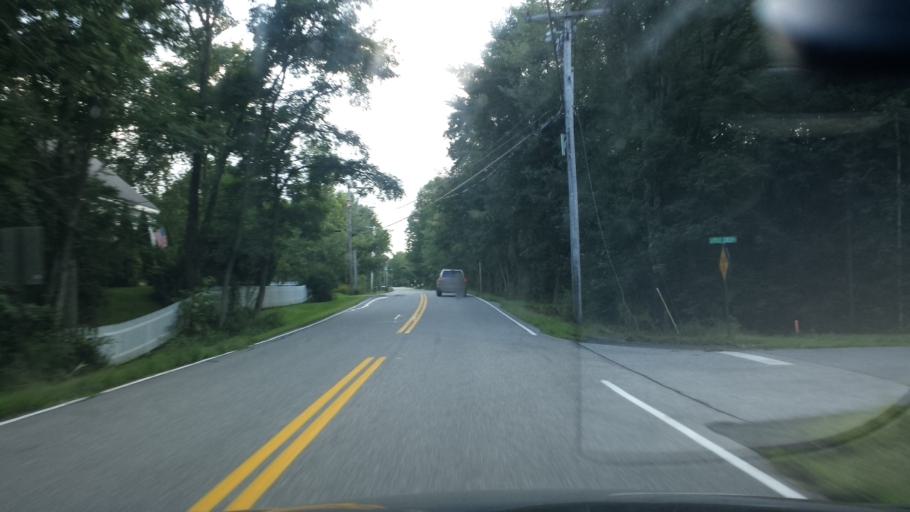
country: US
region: Maine
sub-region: York County
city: Biddeford
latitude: 43.4399
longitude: -70.4442
